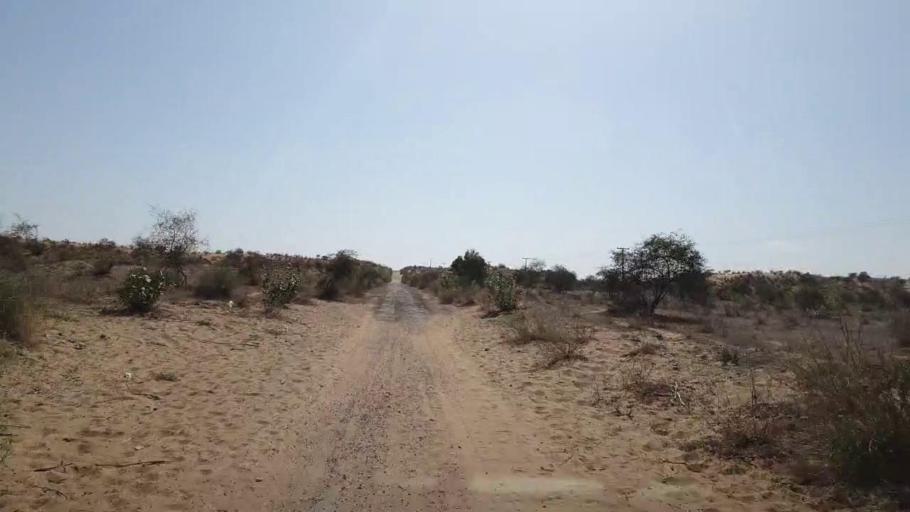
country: PK
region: Sindh
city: Umarkot
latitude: 25.1655
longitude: 70.0424
